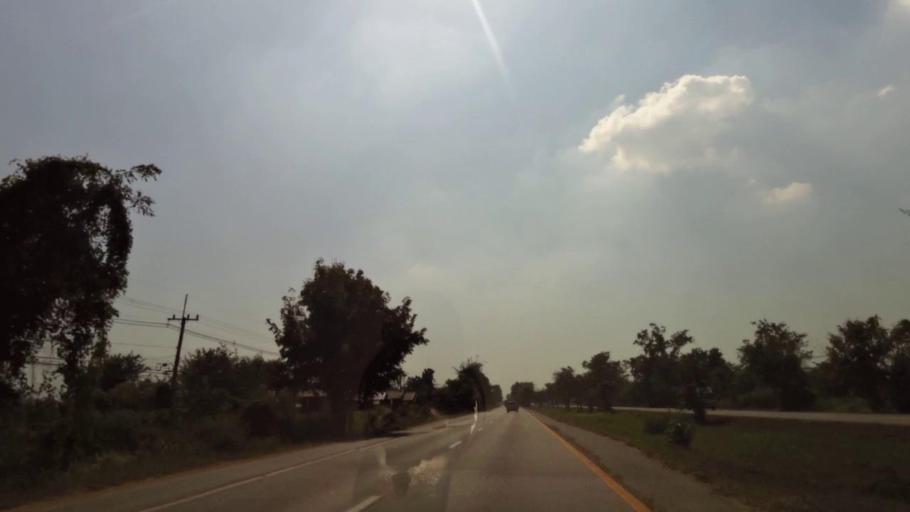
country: TH
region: Phichit
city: Wachira Barami
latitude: 16.5374
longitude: 100.1444
